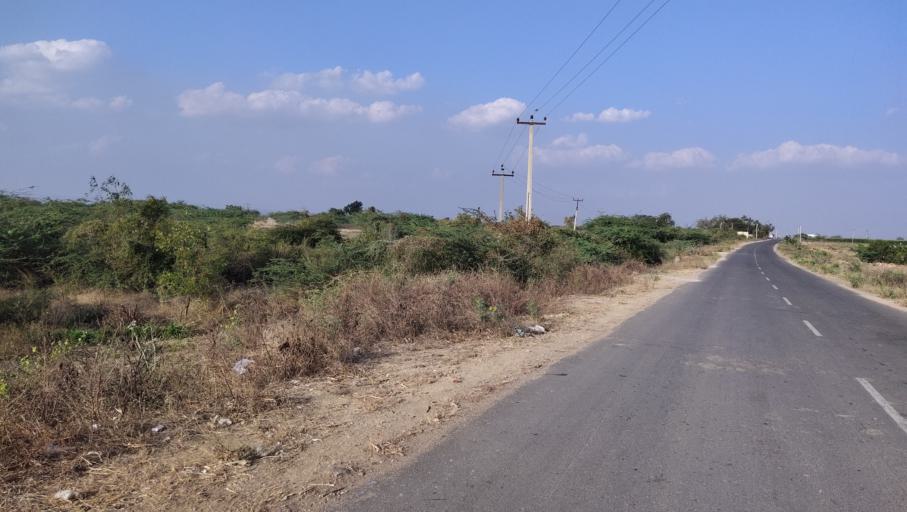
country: IN
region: Andhra Pradesh
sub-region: Anantapur
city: Tadpatri
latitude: 14.9430
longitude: 77.8720
